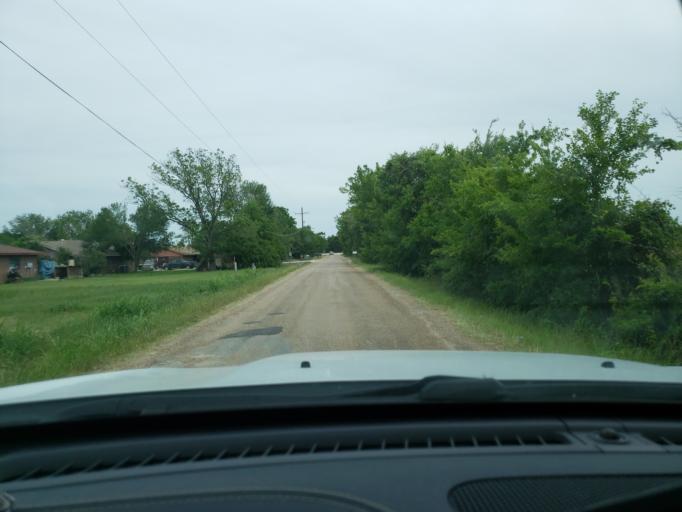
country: US
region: Texas
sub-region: Burleson County
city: Somerville
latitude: 30.3507
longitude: -96.5426
